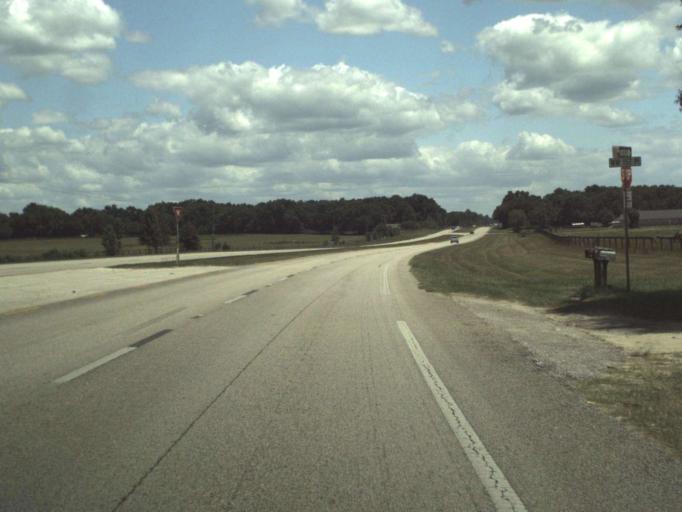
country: US
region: Florida
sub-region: Marion County
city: Citra
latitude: 29.3780
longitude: -82.1775
